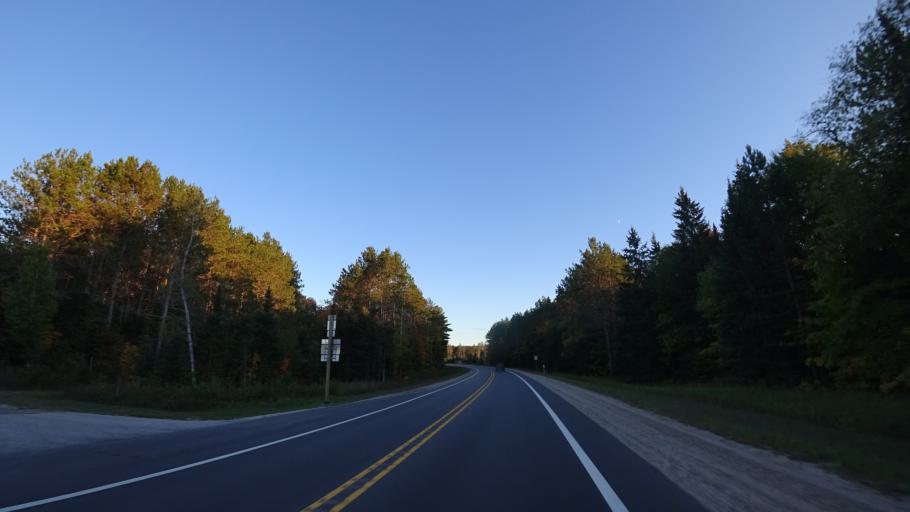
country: US
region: Michigan
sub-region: Luce County
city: Newberry
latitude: 46.3431
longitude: -85.0302
